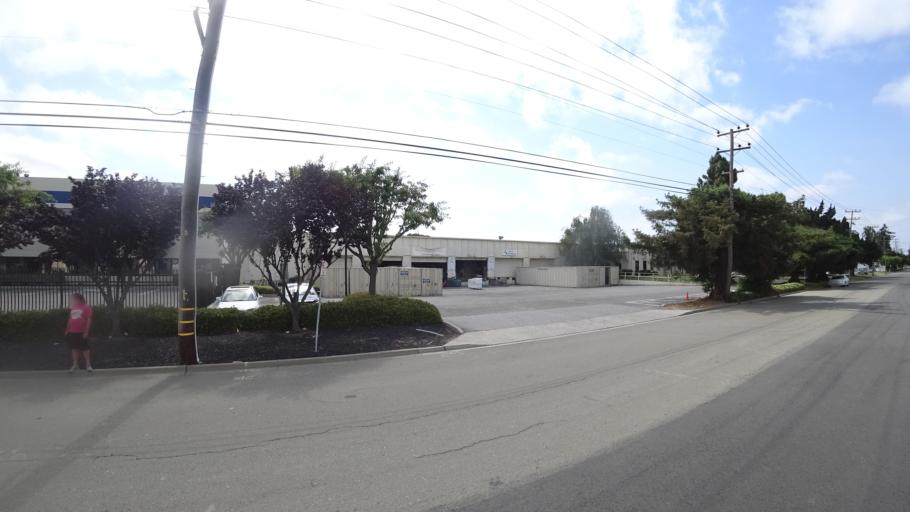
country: US
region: California
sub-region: Alameda County
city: Union City
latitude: 37.6092
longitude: -122.0452
